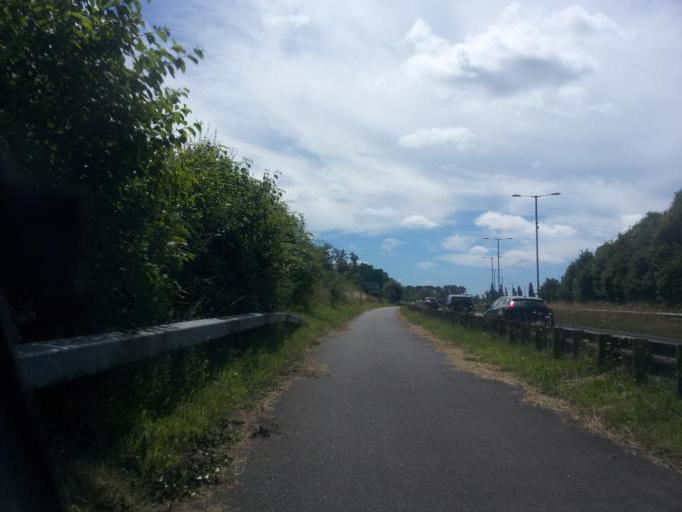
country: GB
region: England
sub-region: Kent
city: Larkfield
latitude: 51.2930
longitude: 0.4208
